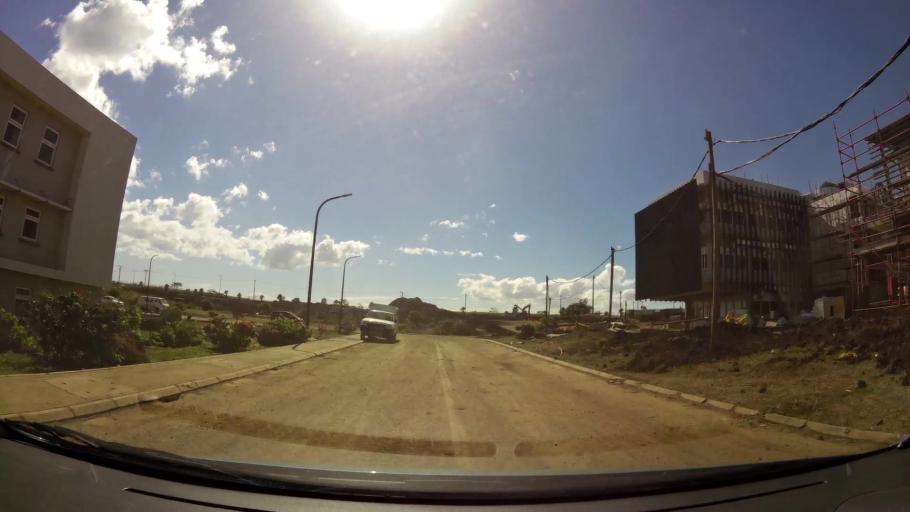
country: MU
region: Black River
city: Cascavelle
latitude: -20.2807
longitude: 57.3943
